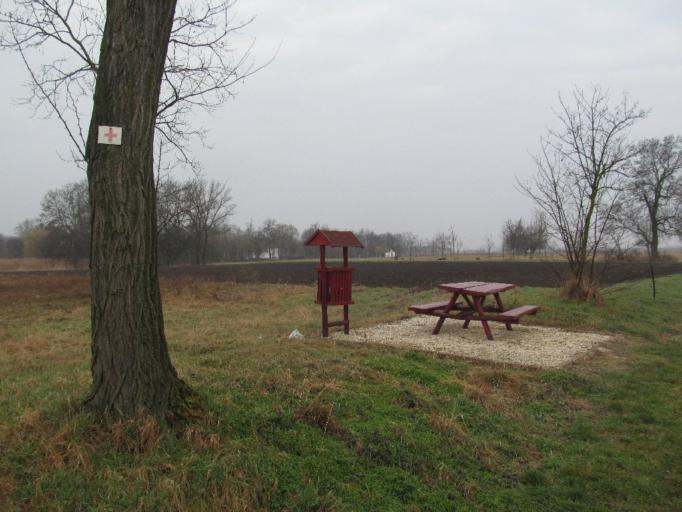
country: HU
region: Csongrad
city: Csengele
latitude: 46.6136
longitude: 19.8484
